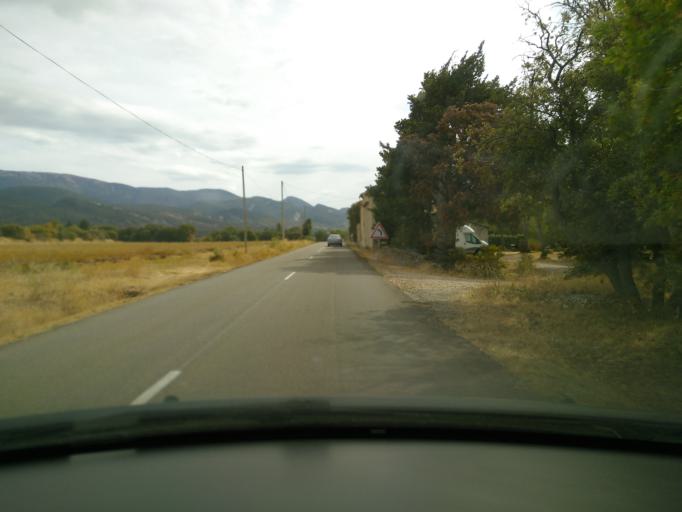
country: FR
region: Rhone-Alpes
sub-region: Departement de la Drome
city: Taulignan
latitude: 44.4427
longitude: 4.9989
